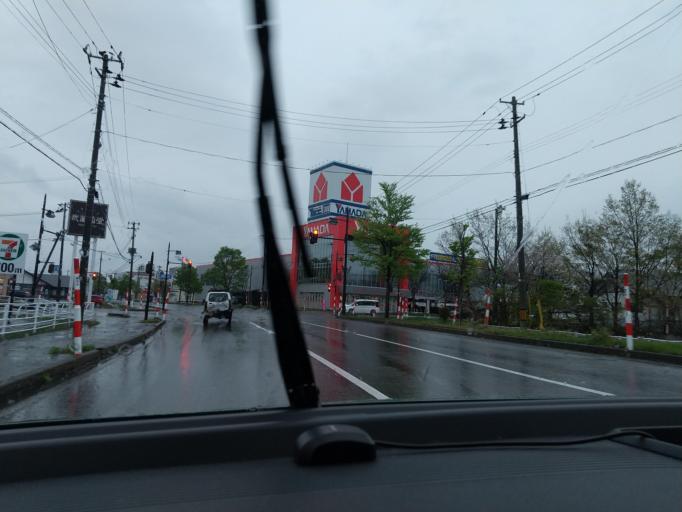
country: JP
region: Akita
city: Yokotemachi
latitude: 39.2964
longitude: 140.5505
